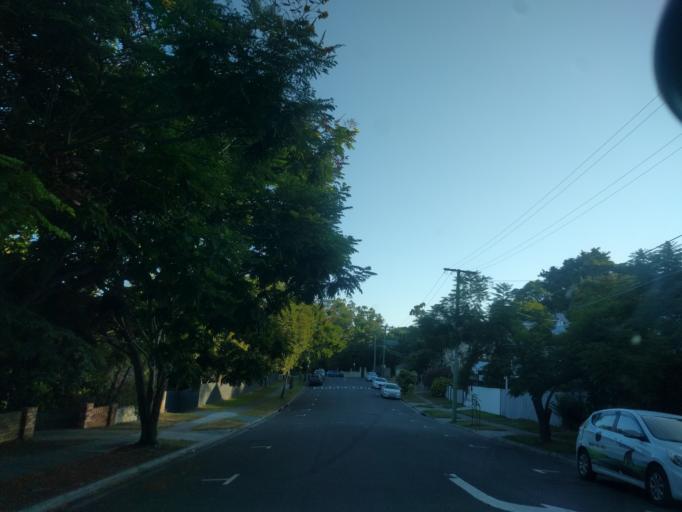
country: AU
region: Queensland
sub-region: Brisbane
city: Spring Hill
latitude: -27.4485
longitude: 153.0213
